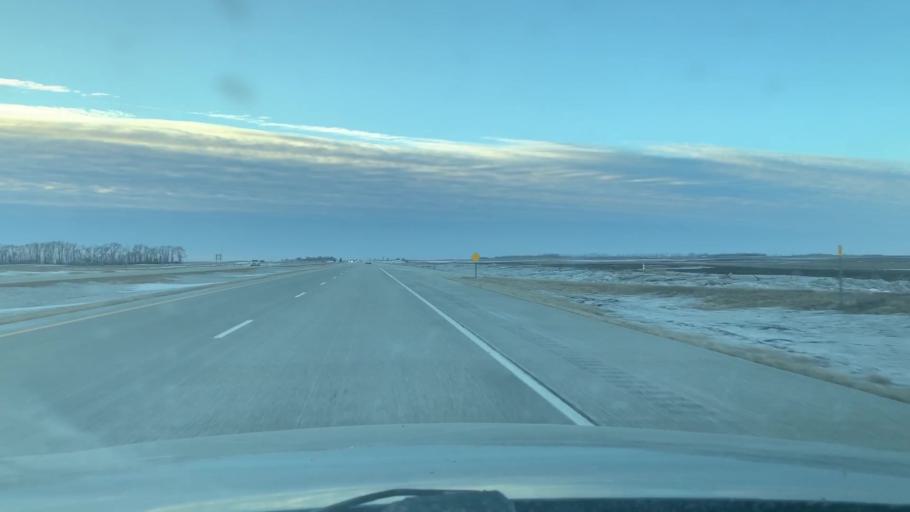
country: US
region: North Dakota
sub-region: Cass County
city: Casselton
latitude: 46.8758
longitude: -97.4960
